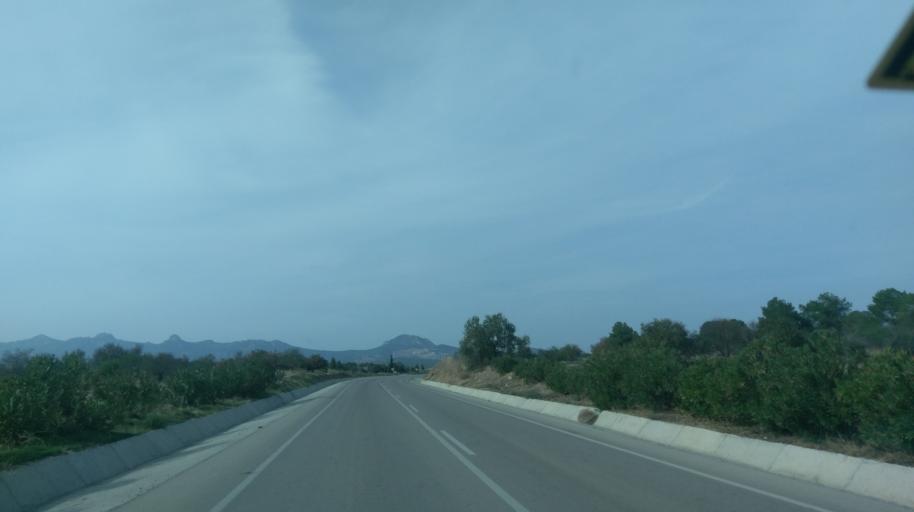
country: CY
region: Ammochostos
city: Leonarisso
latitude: 35.3855
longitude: 34.0136
